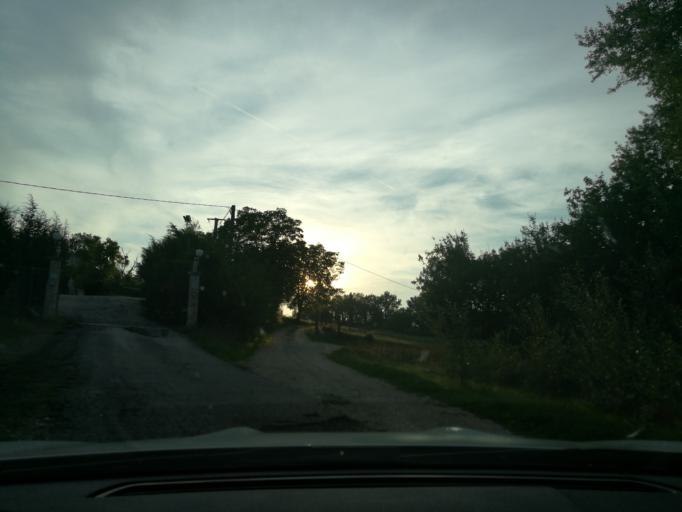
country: IT
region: Umbria
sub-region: Provincia di Terni
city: Acquasparta
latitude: 42.6789
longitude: 12.5452
